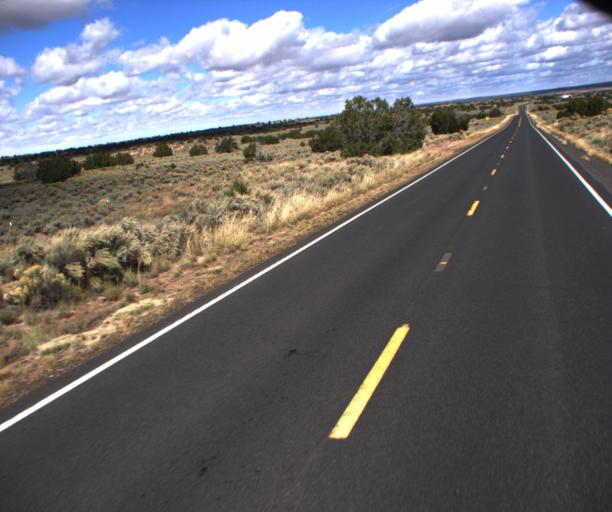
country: US
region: Arizona
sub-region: Apache County
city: Houck
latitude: 35.1574
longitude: -109.3359
